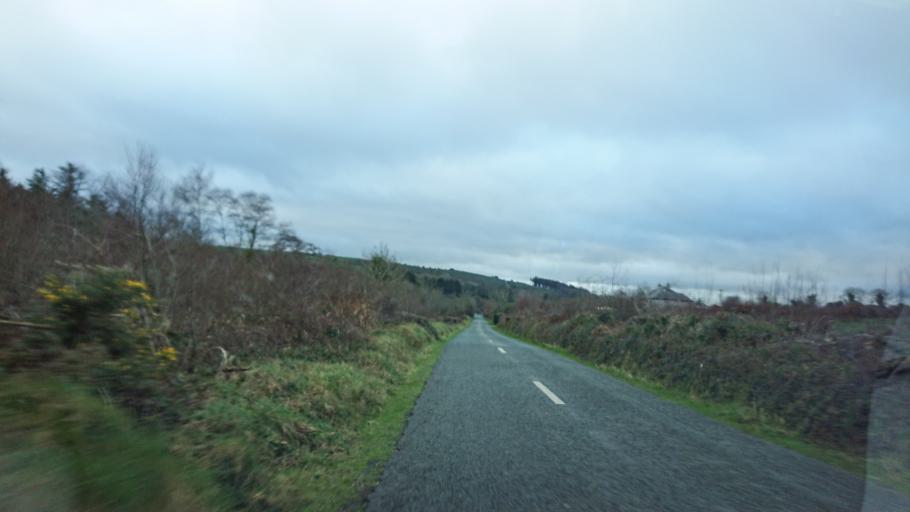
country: IE
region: Munster
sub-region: Waterford
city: Portlaw
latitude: 52.2301
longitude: -7.4102
